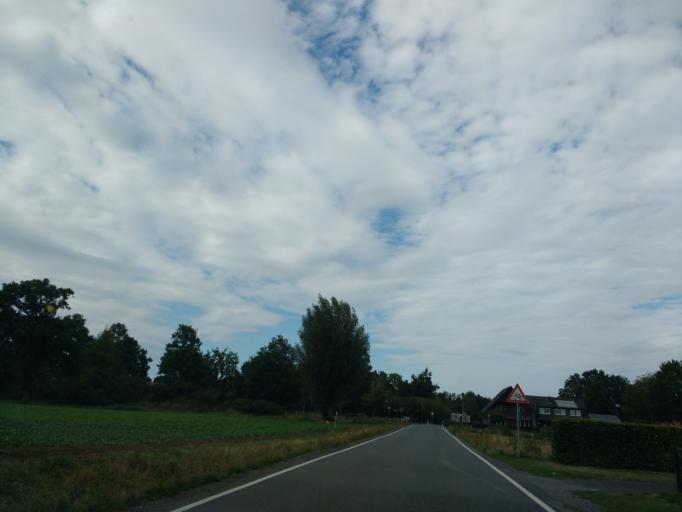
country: DE
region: North Rhine-Westphalia
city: Rietberg
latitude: 51.8148
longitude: 8.4490
